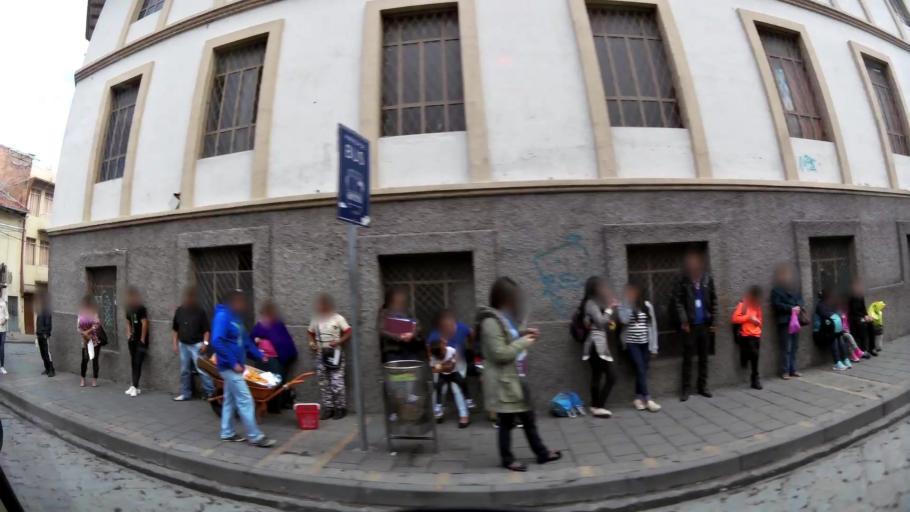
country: EC
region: Azuay
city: Cuenca
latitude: -2.8916
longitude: -79.0050
